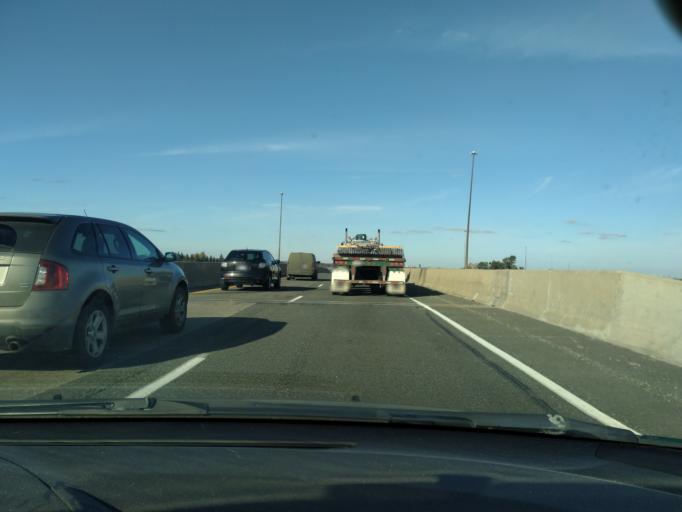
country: CA
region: Ontario
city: Brampton
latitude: 43.5966
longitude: -79.7994
